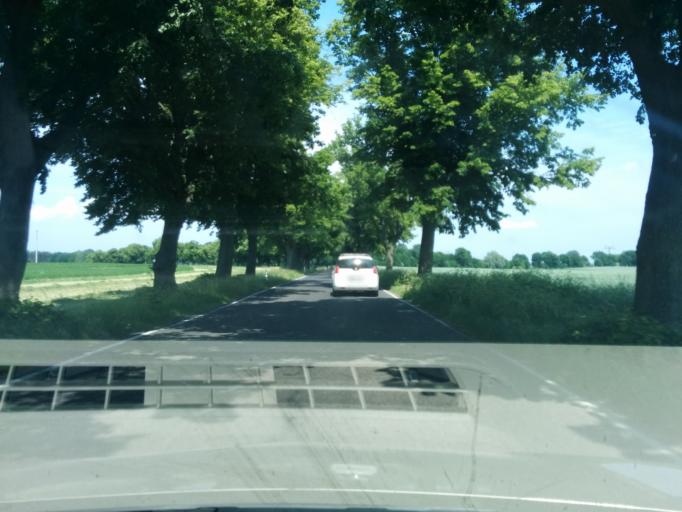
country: DE
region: Brandenburg
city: Bernau bei Berlin
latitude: 52.6409
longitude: 13.5745
